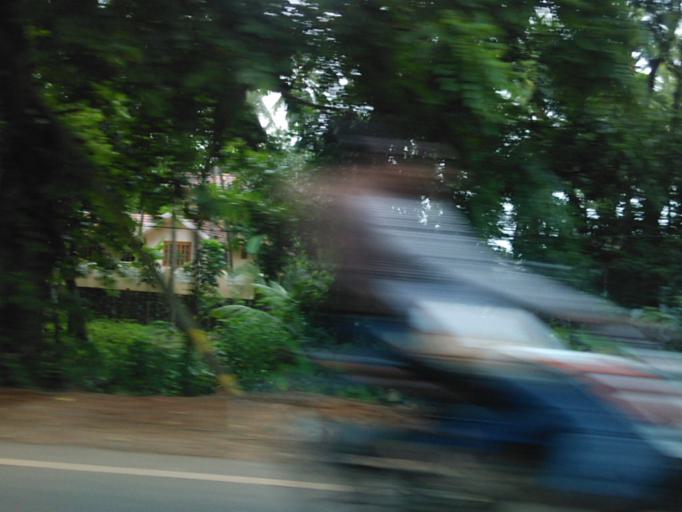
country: IN
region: Kerala
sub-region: Kozhikode
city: Kunnamangalam
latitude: 11.2968
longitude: 75.8445
